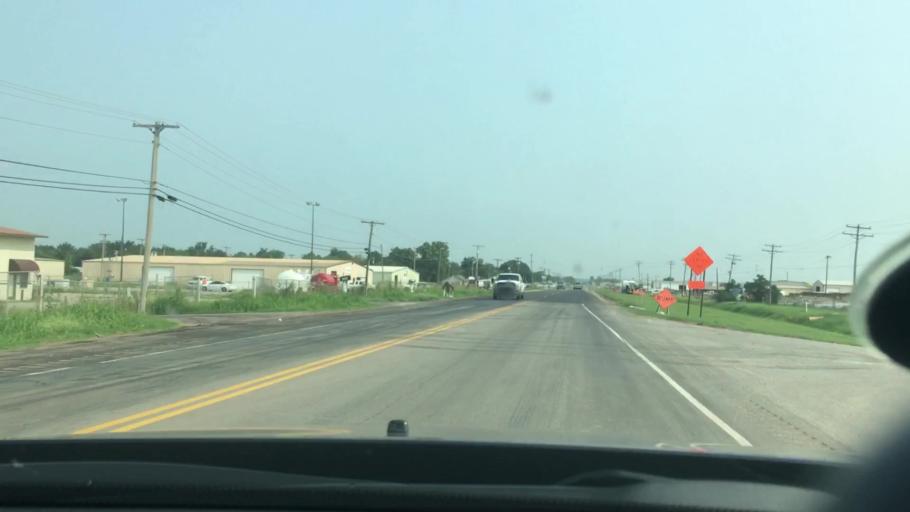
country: US
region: Oklahoma
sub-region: Garvin County
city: Lindsay
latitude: 34.8237
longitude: -97.5983
